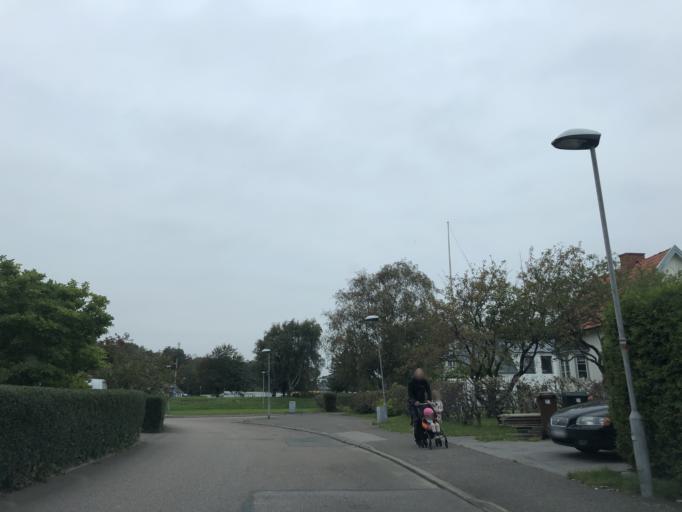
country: SE
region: Vaestra Goetaland
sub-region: Goteborg
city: Majorna
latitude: 57.6542
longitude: 11.8761
